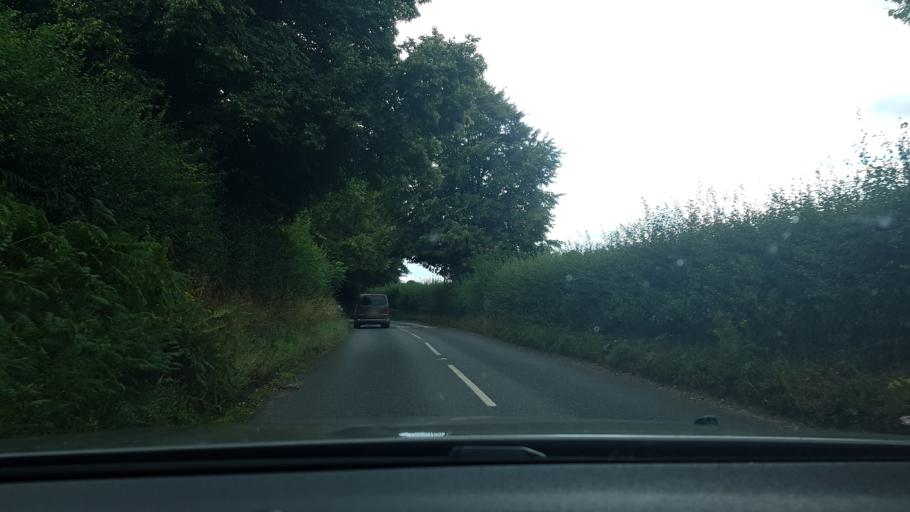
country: GB
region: England
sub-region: West Berkshire
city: Basildon
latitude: 51.4691
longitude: -1.1744
